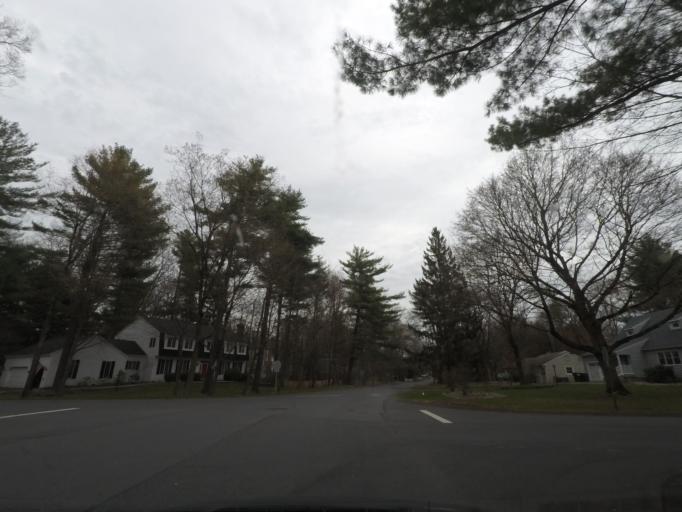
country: US
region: New York
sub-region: Albany County
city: Delmar
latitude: 42.6106
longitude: -73.8393
